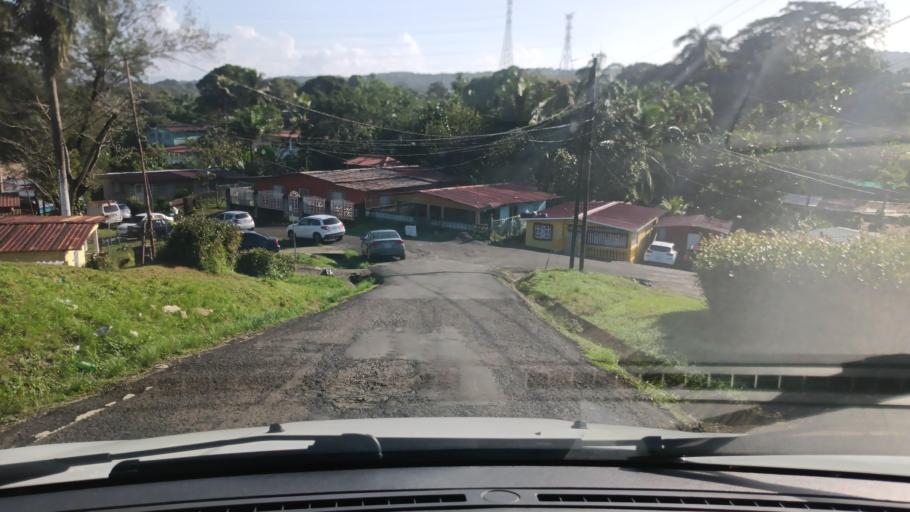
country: PA
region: Colon
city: Sabanitas
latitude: 9.3430
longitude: -79.8030
